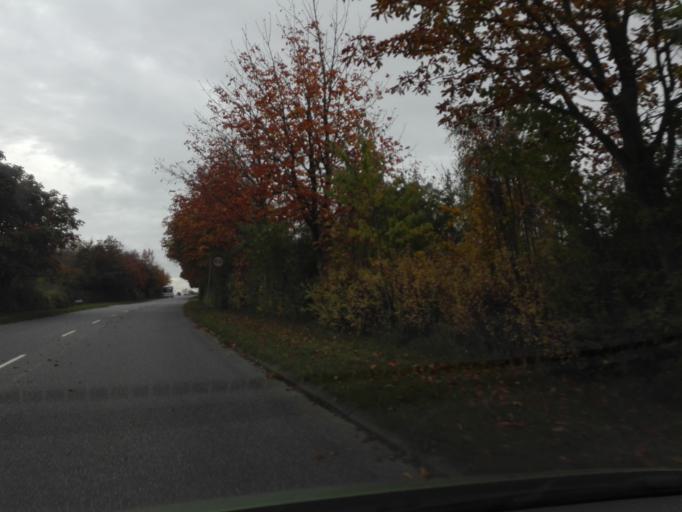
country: DK
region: Central Jutland
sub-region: Arhus Kommune
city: Kolt
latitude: 56.1044
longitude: 10.0695
